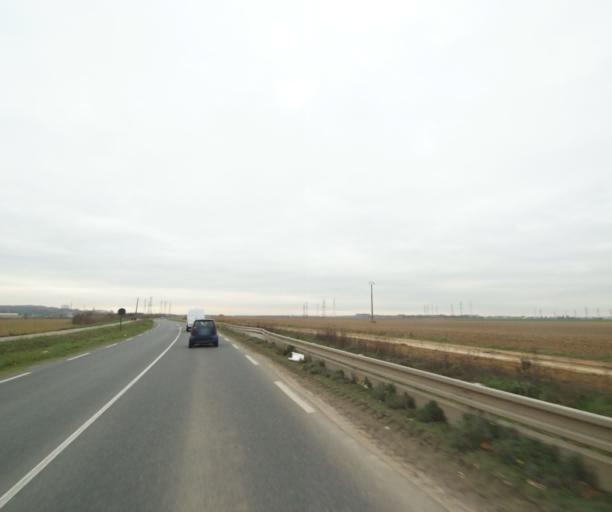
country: FR
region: Ile-de-France
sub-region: Departement du Val-d'Oise
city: Villiers-le-Bel
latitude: 49.0094
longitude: 2.4227
